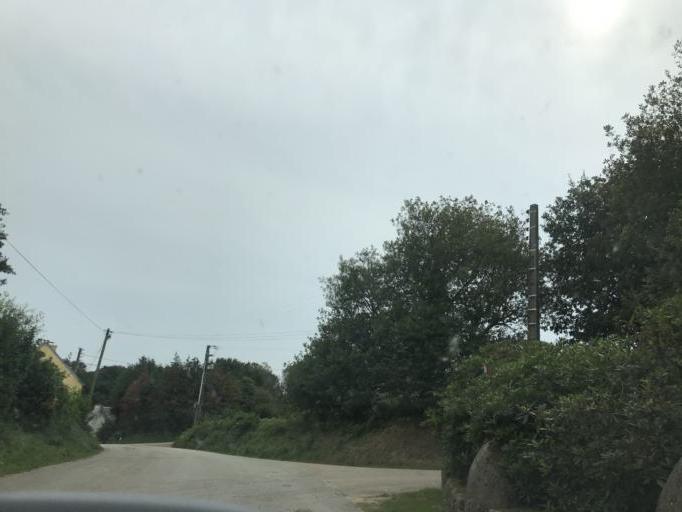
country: FR
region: Brittany
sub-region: Departement du Finistere
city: Plouneour-Menez
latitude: 48.3687
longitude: -3.8627
